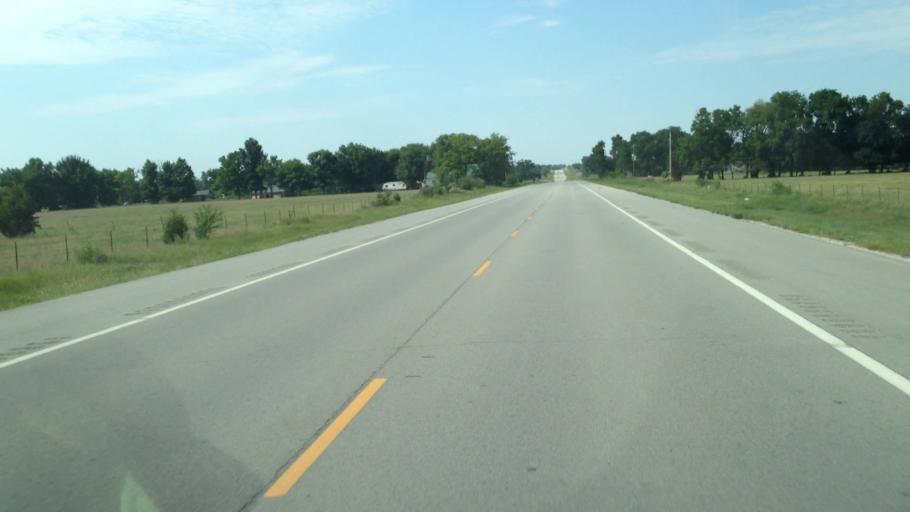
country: US
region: Kansas
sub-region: Labette County
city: Parsons
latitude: 37.2631
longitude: -95.2672
